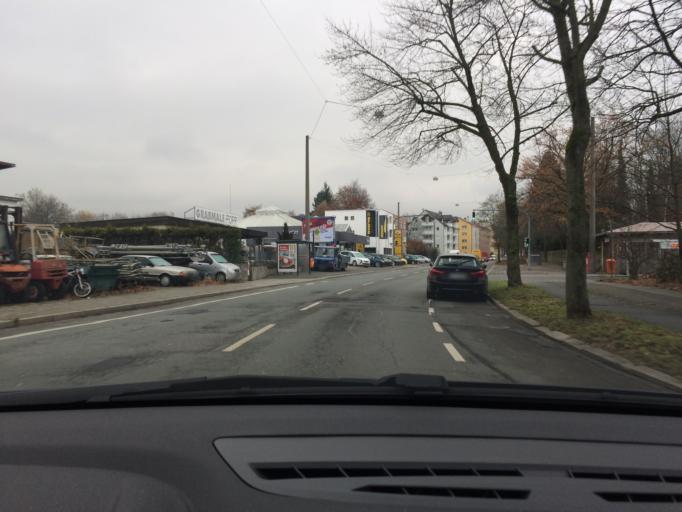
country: DE
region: Bavaria
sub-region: Regierungsbezirk Mittelfranken
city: Wetzendorf
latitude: 49.4664
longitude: 11.0400
